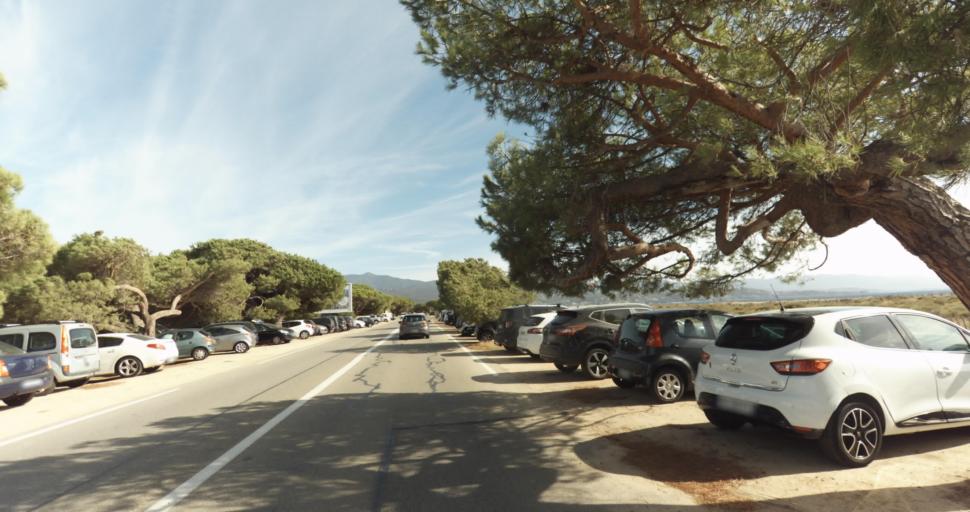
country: FR
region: Corsica
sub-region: Departement de la Corse-du-Sud
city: Ajaccio
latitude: 41.9221
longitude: 8.7861
